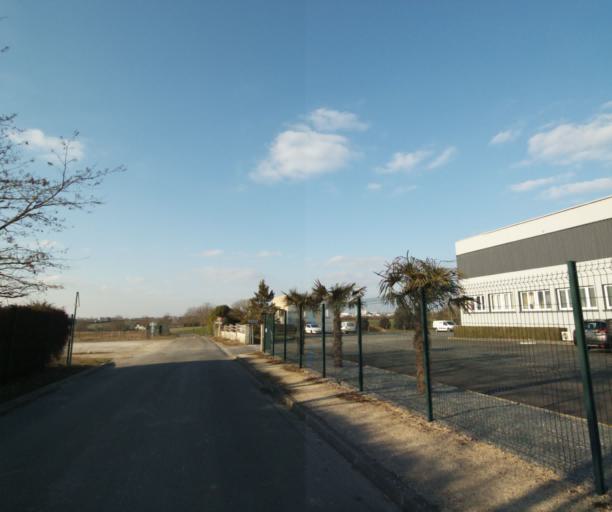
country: FR
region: Poitou-Charentes
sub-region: Departement des Deux-Sevres
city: Aiffres
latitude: 46.3186
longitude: -0.4068
